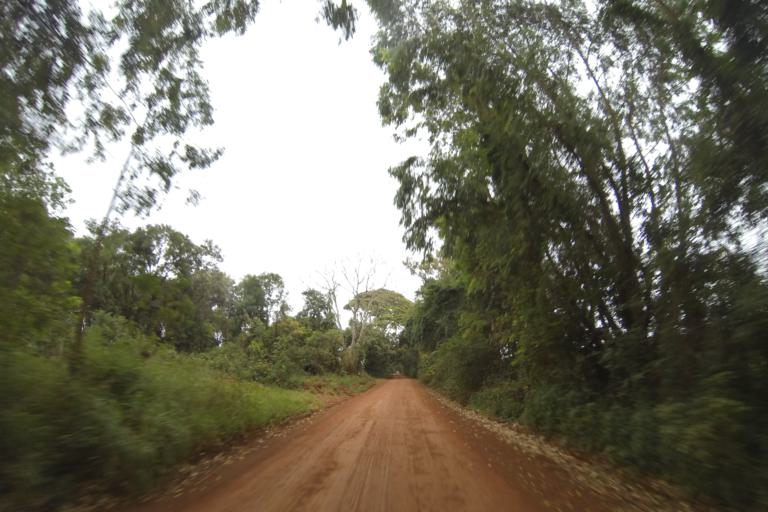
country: BR
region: Minas Gerais
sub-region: Campos Altos
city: Campos Altos
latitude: -19.8165
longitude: -46.3374
